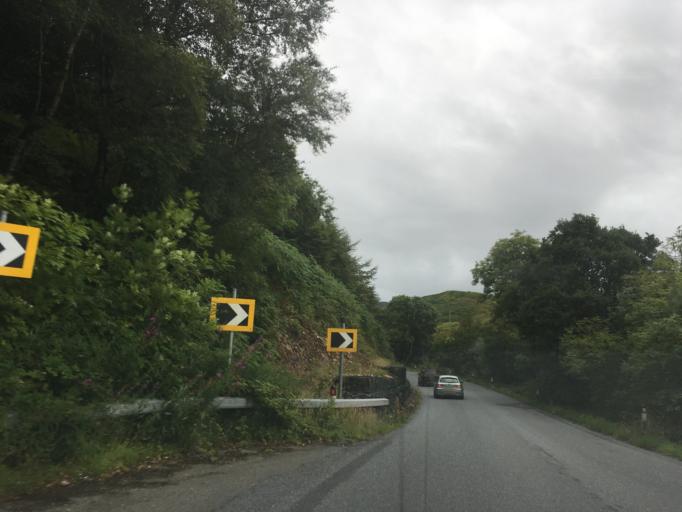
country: GB
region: Scotland
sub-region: Argyll and Bute
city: Oban
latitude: 56.2679
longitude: -5.4792
